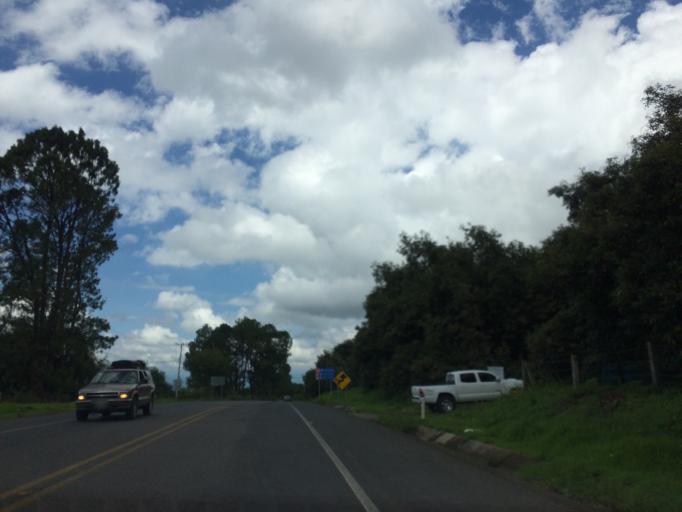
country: MX
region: Michoacan
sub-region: Uruapan
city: Nuevo Zirosto
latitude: 19.5469
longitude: -102.3338
